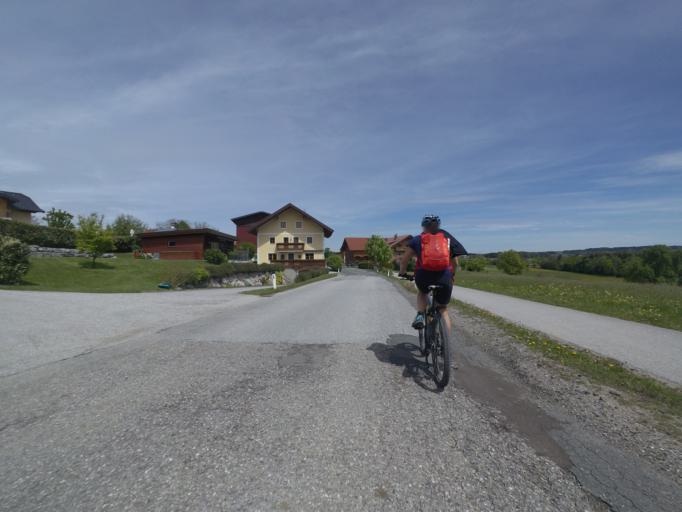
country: AT
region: Salzburg
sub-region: Politischer Bezirk Salzburg-Umgebung
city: Berndorf bei Salzburg
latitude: 47.9945
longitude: 13.0874
